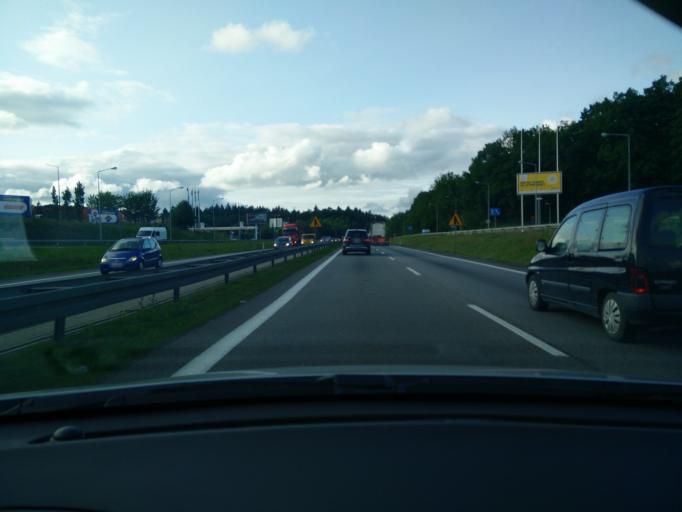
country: PL
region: Pomeranian Voivodeship
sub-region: Gdynia
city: Wielki Kack
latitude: 54.4319
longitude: 18.4879
